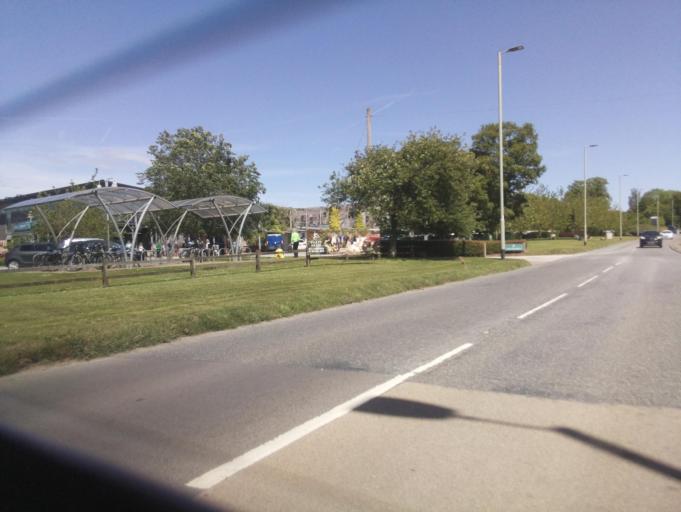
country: GB
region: England
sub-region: Devon
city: Topsham
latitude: 50.6851
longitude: -3.4490
